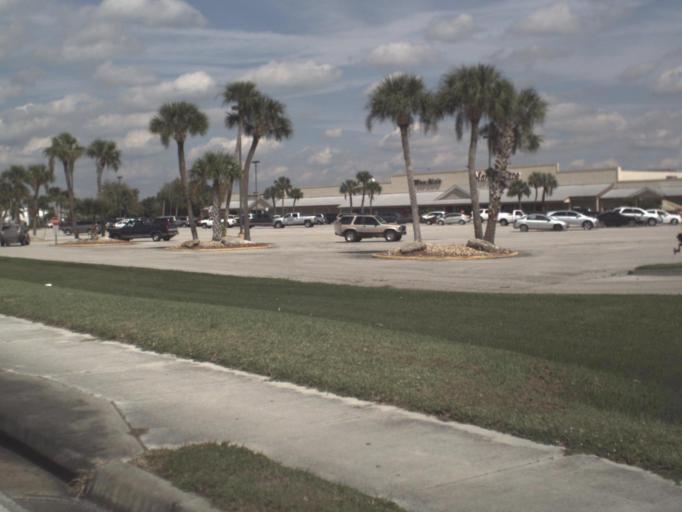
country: US
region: Florida
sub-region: Okeechobee County
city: Okeechobee
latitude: 27.2123
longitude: -80.8298
